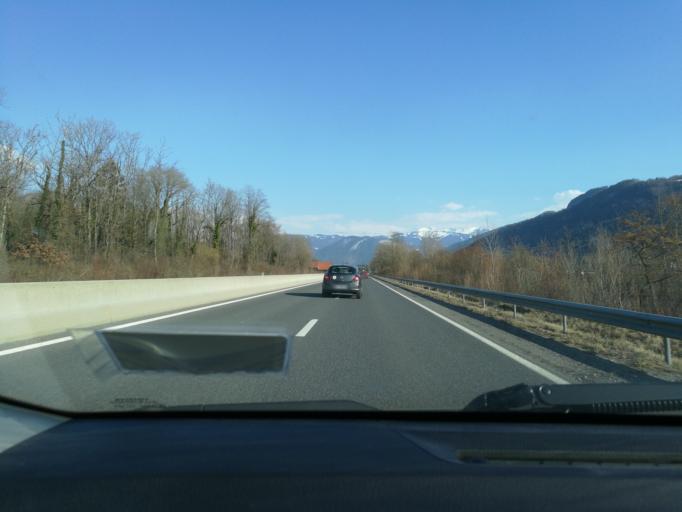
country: FR
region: Rhone-Alpes
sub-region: Departement de la Haute-Savoie
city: Mont-Saxonnex
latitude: 46.0729
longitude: 6.4649
